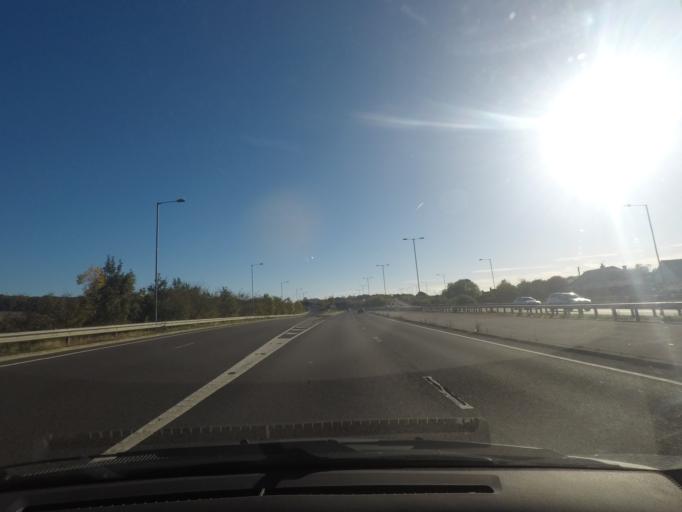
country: GB
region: England
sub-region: East Riding of Yorkshire
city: North Ferriby
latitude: 53.7252
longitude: -0.5263
